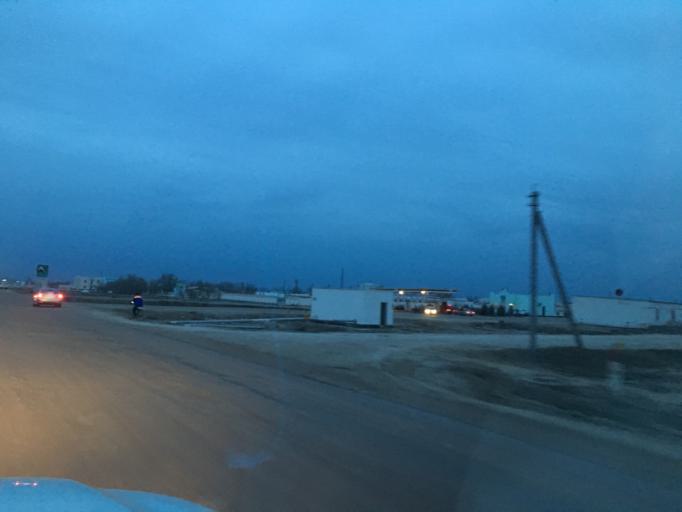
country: TM
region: Dasoguz
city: Yylanly
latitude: 41.8908
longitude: 59.6174
